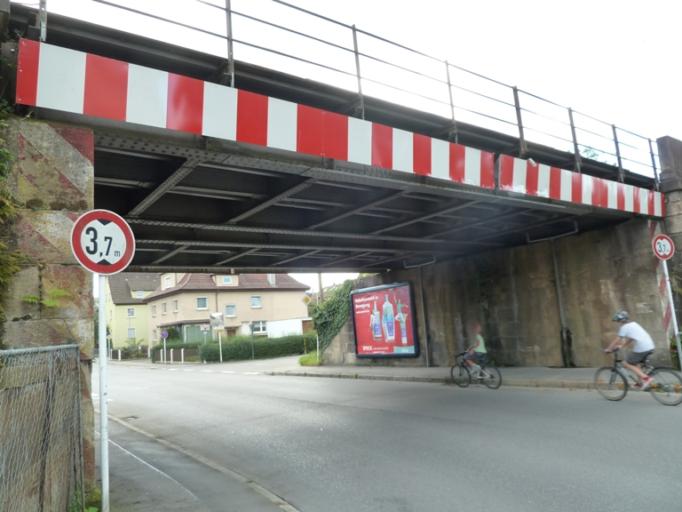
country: DE
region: Baden-Wuerttemberg
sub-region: Tuebingen Region
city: Reutlingen
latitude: 48.4968
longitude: 9.1744
